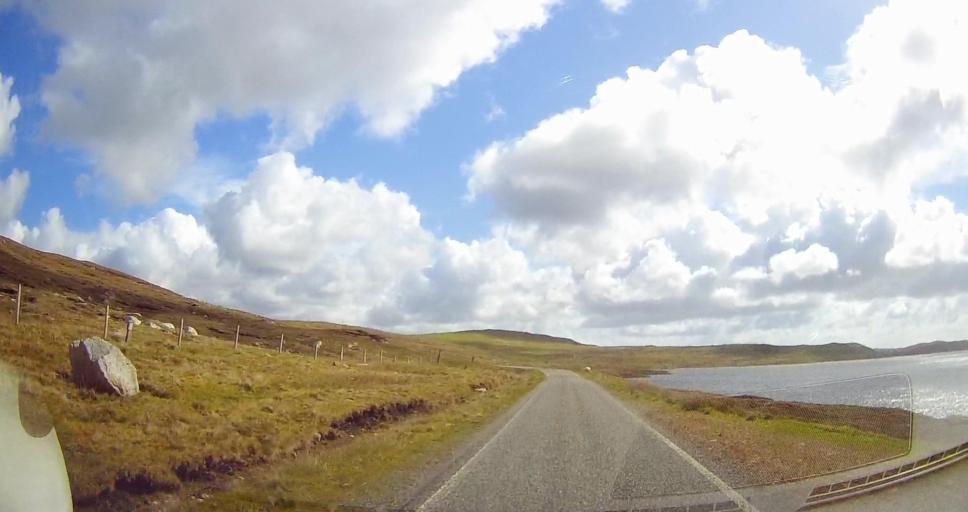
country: GB
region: Scotland
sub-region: Shetland Islands
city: Lerwick
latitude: 60.4944
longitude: -1.3916
